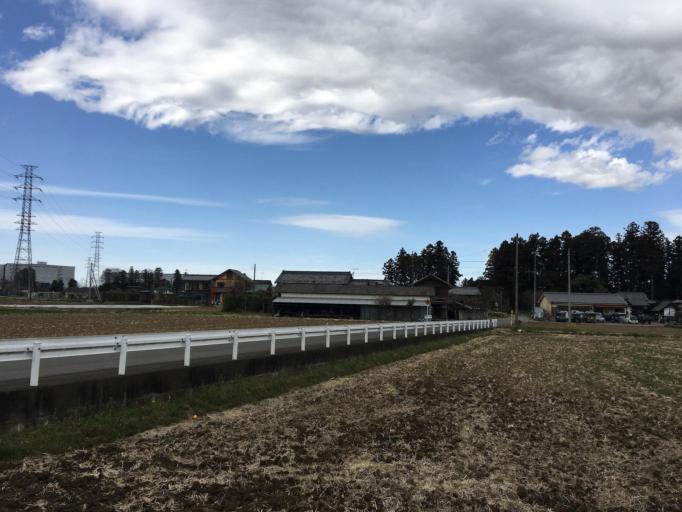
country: JP
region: Saitama
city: Ogawa
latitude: 36.1112
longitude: 139.2603
